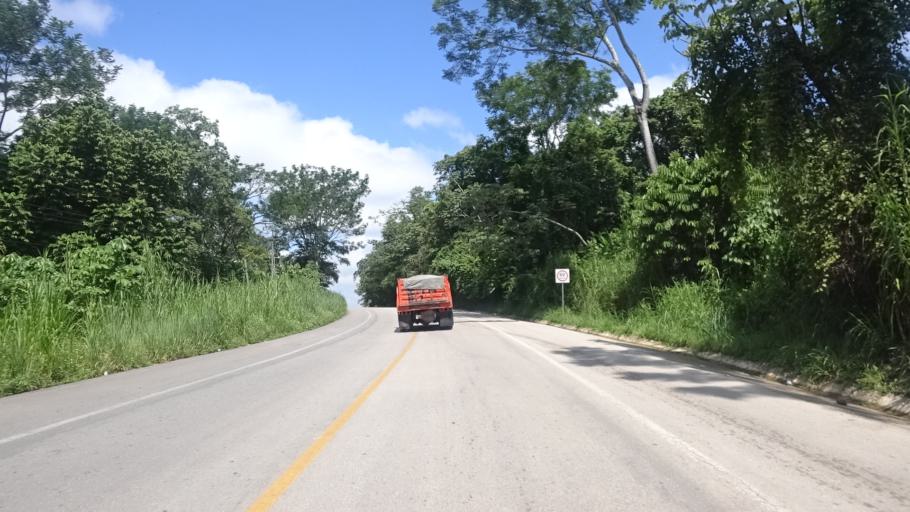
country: MX
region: Chiapas
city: Palenque
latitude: 17.4984
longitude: -91.9884
